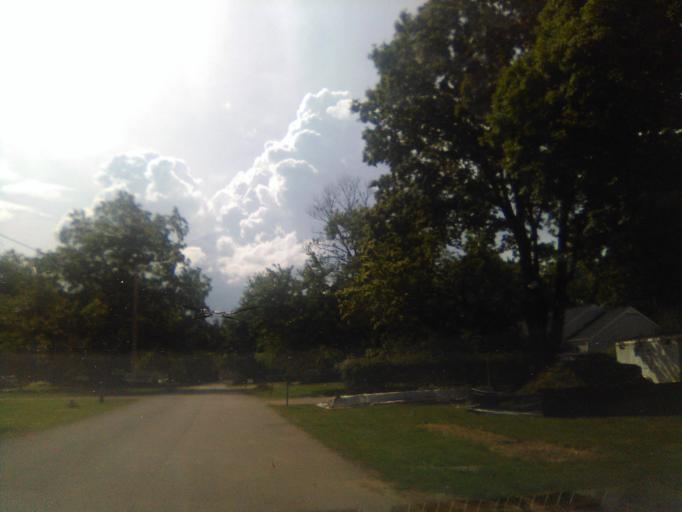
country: US
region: Tennessee
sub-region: Davidson County
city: Belle Meade
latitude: 36.0952
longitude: -86.8722
